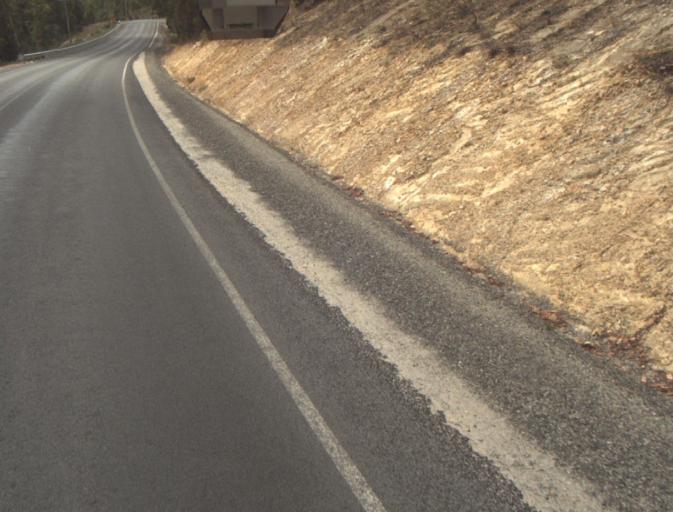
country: AU
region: Tasmania
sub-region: Dorset
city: Bridport
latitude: -41.1661
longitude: 147.2570
